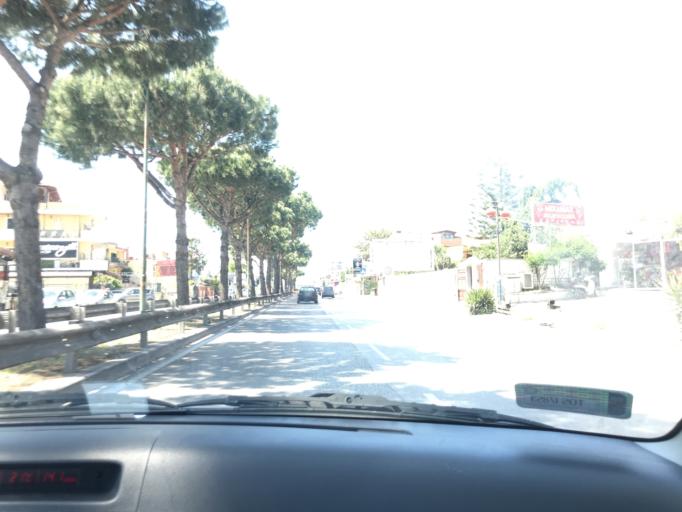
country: IT
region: Campania
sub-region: Provincia di Napoli
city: Villaricca
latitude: 40.9202
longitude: 14.1806
